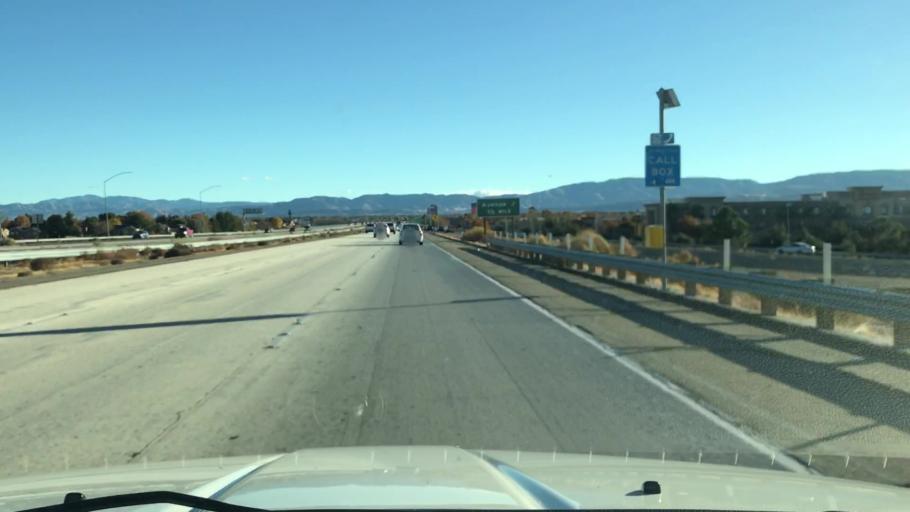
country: US
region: California
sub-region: Los Angeles County
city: Lancaster
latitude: 34.7030
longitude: -118.1703
